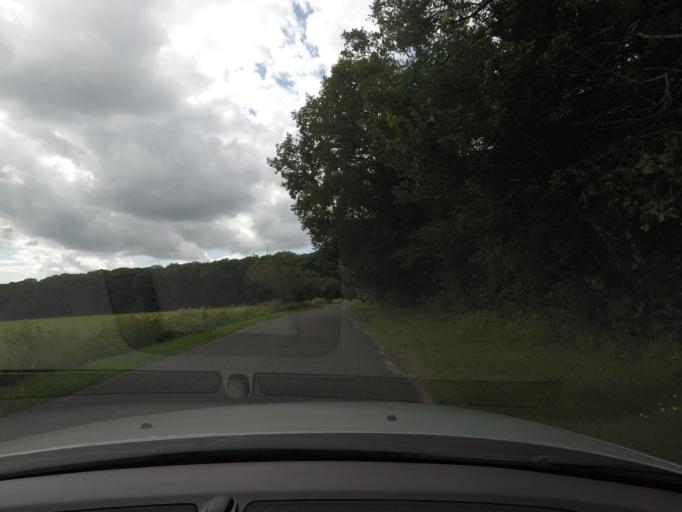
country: FR
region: Haute-Normandie
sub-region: Departement de l'Eure
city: Les Andelys
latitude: 49.2372
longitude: 1.4127
